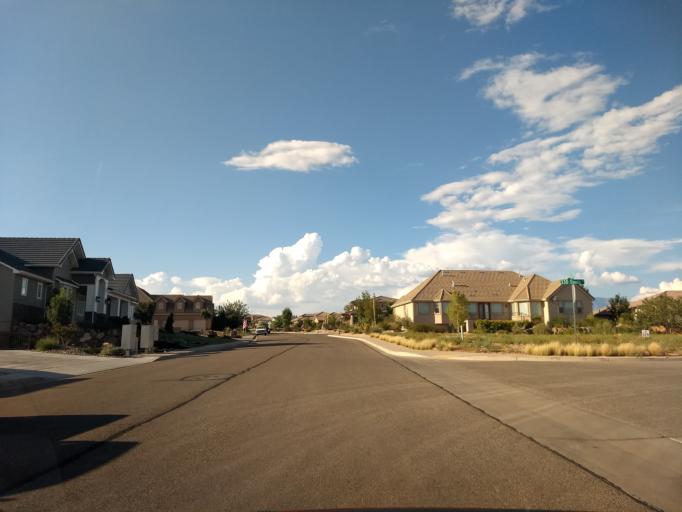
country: US
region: Utah
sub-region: Washington County
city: Saint George
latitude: 37.1023
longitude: -113.5484
